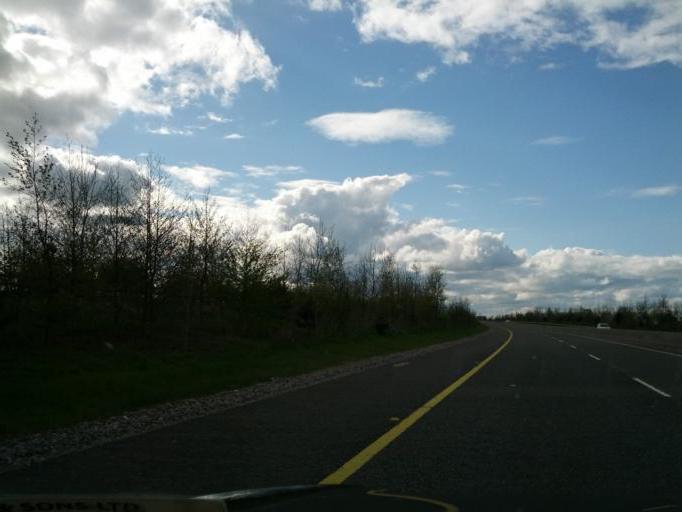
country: IE
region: Leinster
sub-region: An Iarmhi
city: Kilbeggan
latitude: 53.3694
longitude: -7.5347
